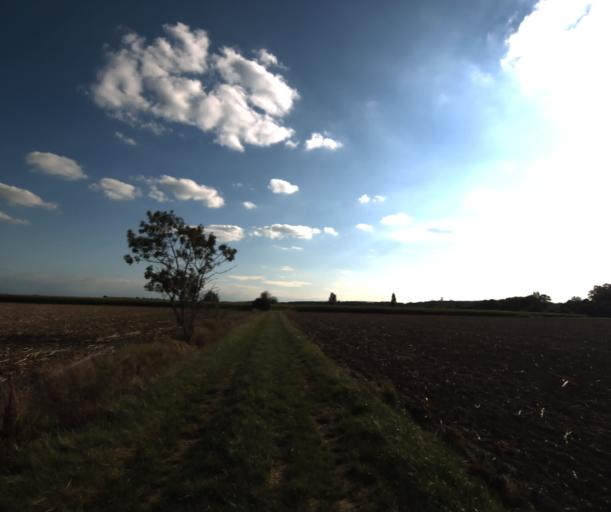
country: FR
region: Midi-Pyrenees
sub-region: Departement de la Haute-Garonne
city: Labastidette
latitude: 43.4511
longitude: 1.2478
